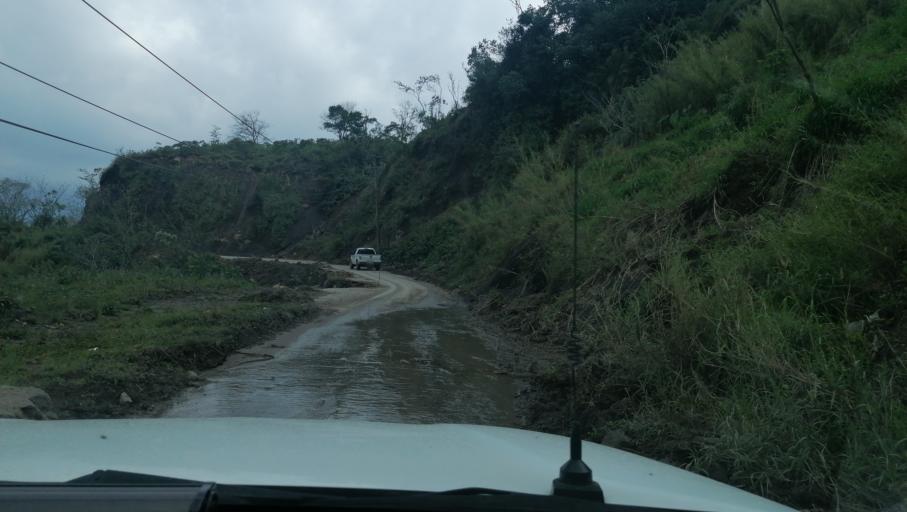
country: MX
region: Chiapas
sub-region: Ocotepec
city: San Pablo Huacano
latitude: 17.2597
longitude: -93.2685
